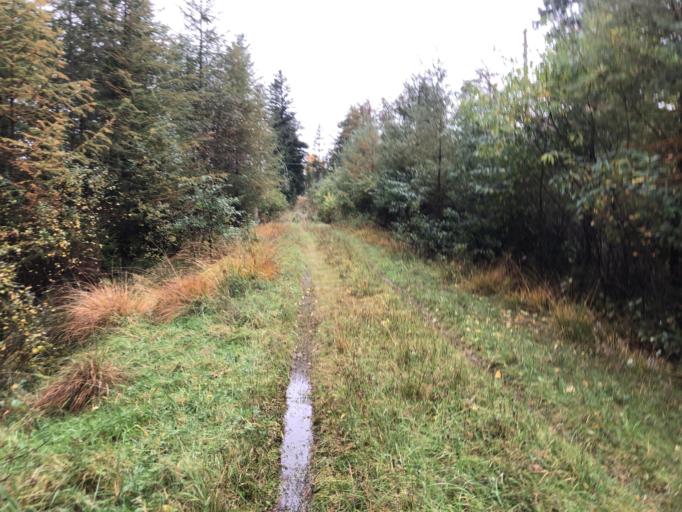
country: DK
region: Central Jutland
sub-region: Holstebro Kommune
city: Ulfborg
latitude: 56.2698
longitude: 8.4371
